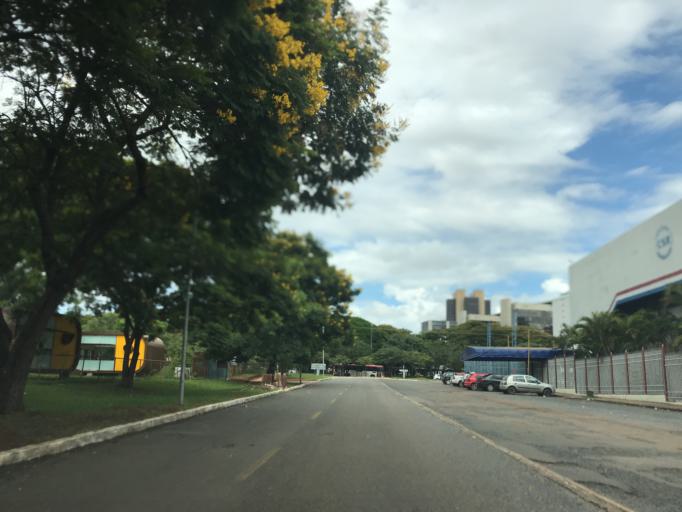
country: BR
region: Federal District
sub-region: Brasilia
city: Brasilia
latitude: -15.8081
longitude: -47.8803
